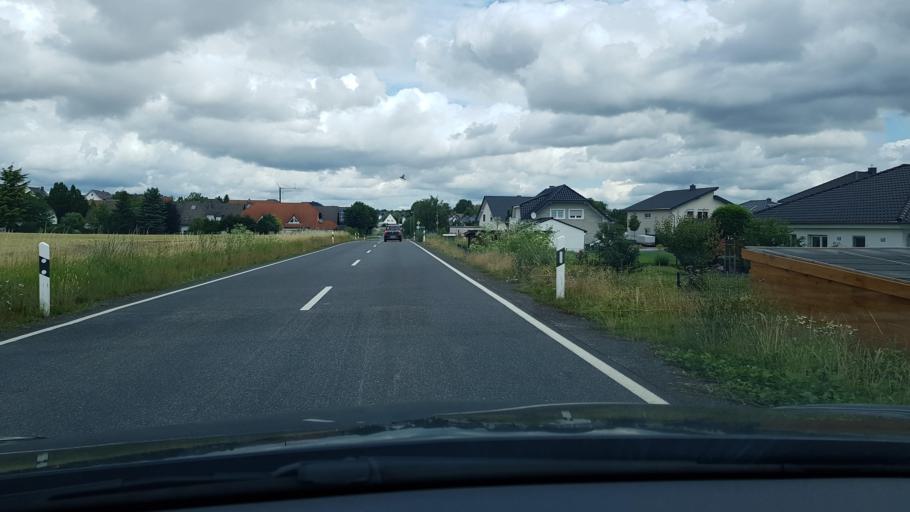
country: DE
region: Rheinland-Pfalz
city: Polch
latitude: 50.2909
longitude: 7.3083
